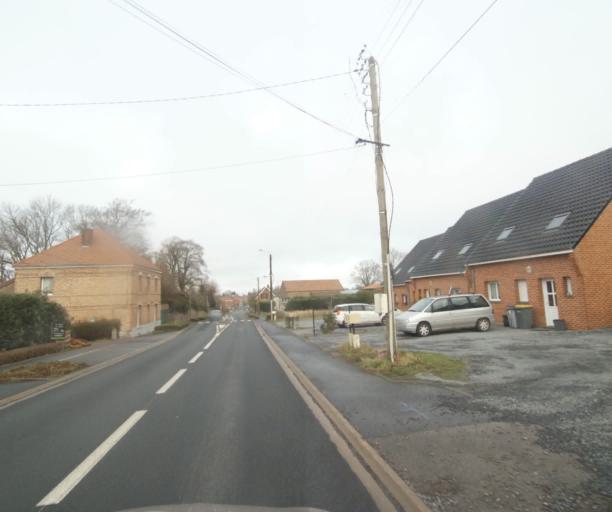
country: FR
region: Nord-Pas-de-Calais
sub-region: Departement du Nord
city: Vendegies-sur-Ecaillon
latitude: 50.2822
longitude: 3.5148
